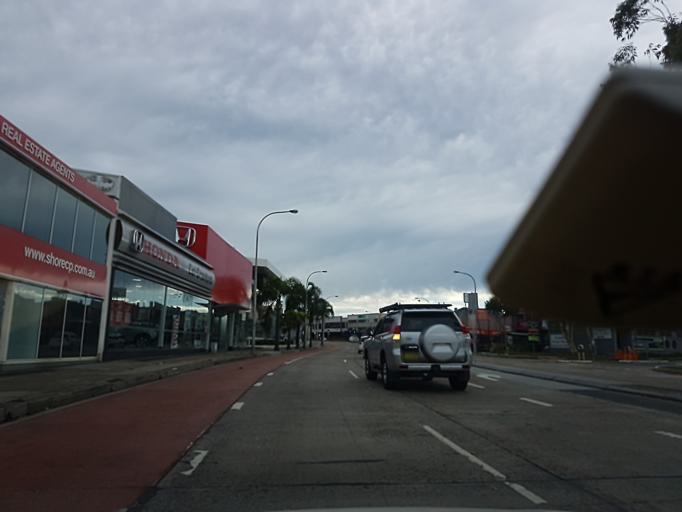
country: AU
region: New South Wales
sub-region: Warringah
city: Brookvale
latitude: -33.7653
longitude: 151.2701
